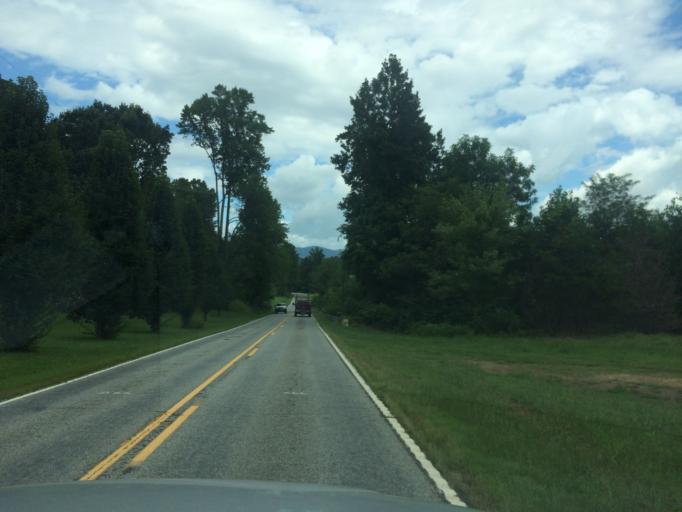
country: US
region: North Carolina
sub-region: Rutherford County
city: Lake Lure
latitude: 35.3615
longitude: -82.1808
